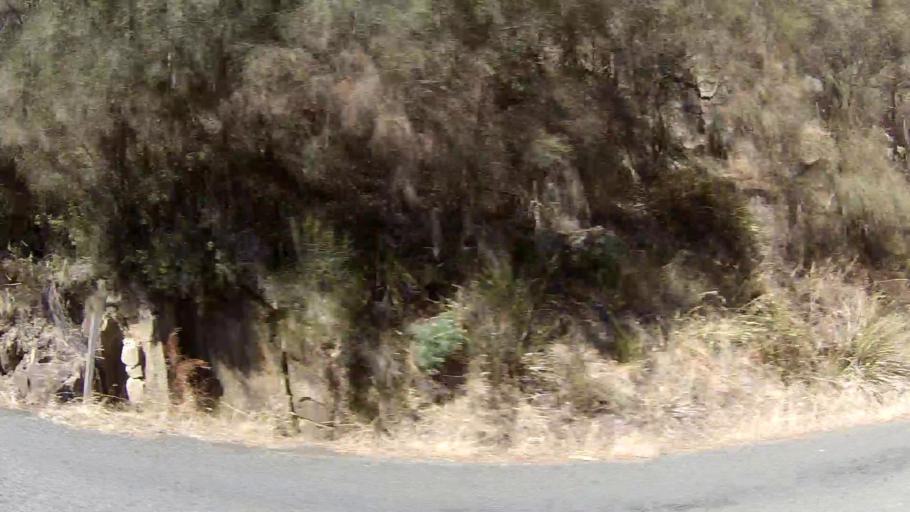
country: AU
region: Tasmania
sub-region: Sorell
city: Sorell
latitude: -42.5687
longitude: 147.8228
